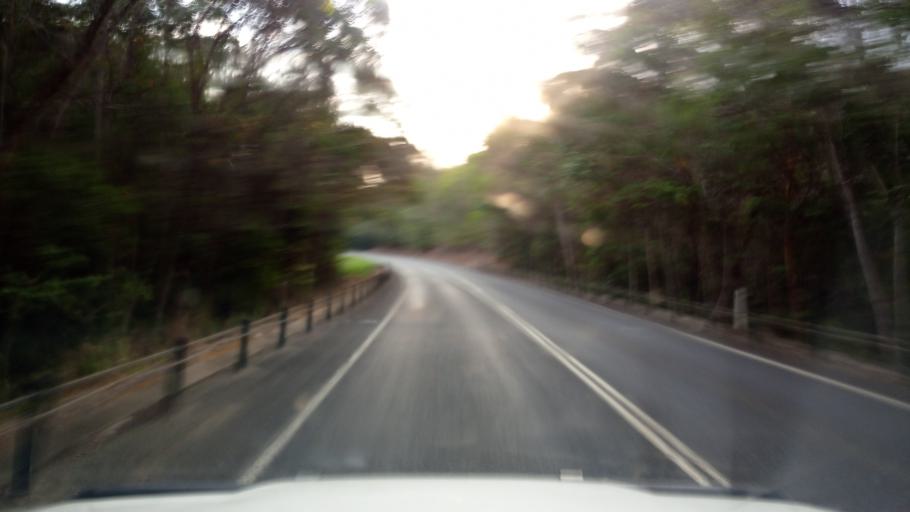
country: AU
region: Queensland
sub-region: Tablelands
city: Kuranda
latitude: -16.8466
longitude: 145.6044
